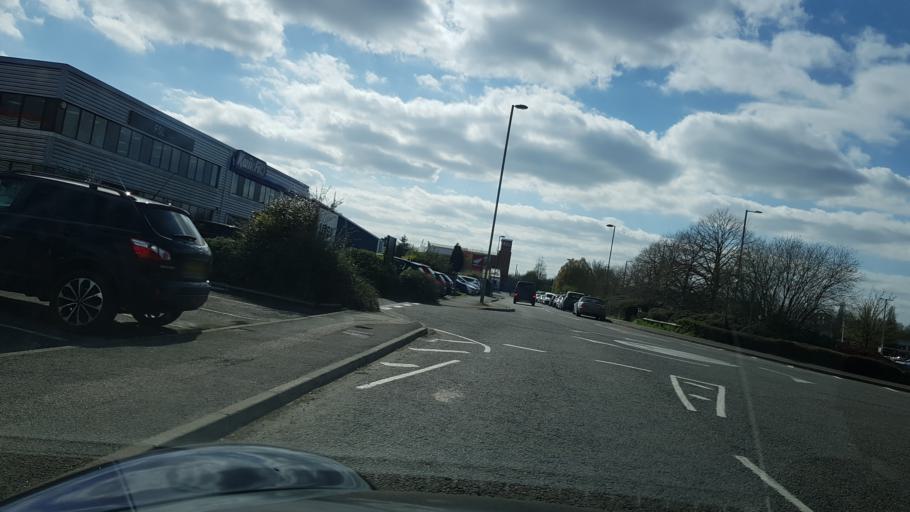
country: GB
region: England
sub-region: Surrey
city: Hale
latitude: 51.2232
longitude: -0.7739
